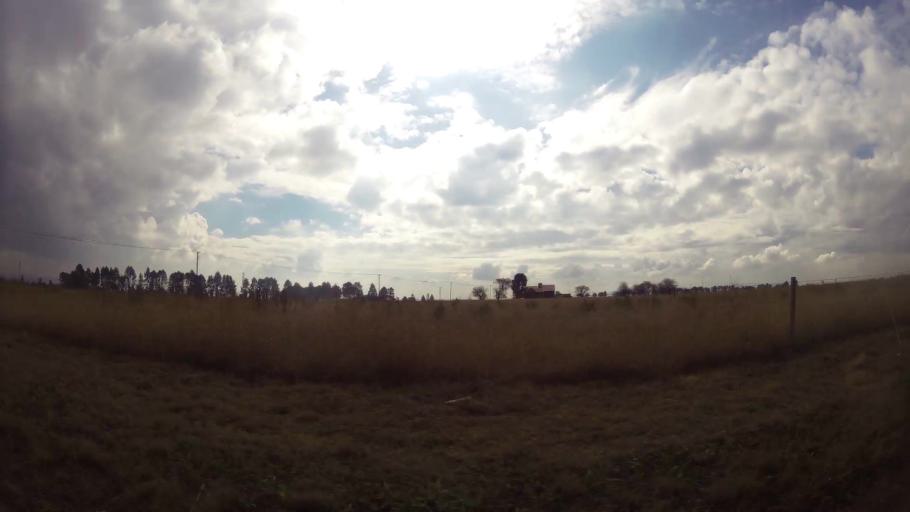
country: ZA
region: Gauteng
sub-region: Sedibeng District Municipality
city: Meyerton
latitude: -26.5988
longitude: 28.0457
